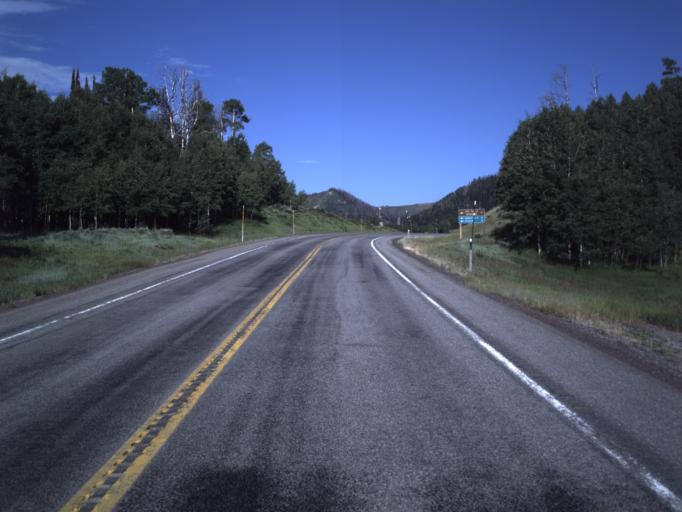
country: US
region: Utah
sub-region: Sanpete County
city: Fairview
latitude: 39.5823
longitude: -111.2486
